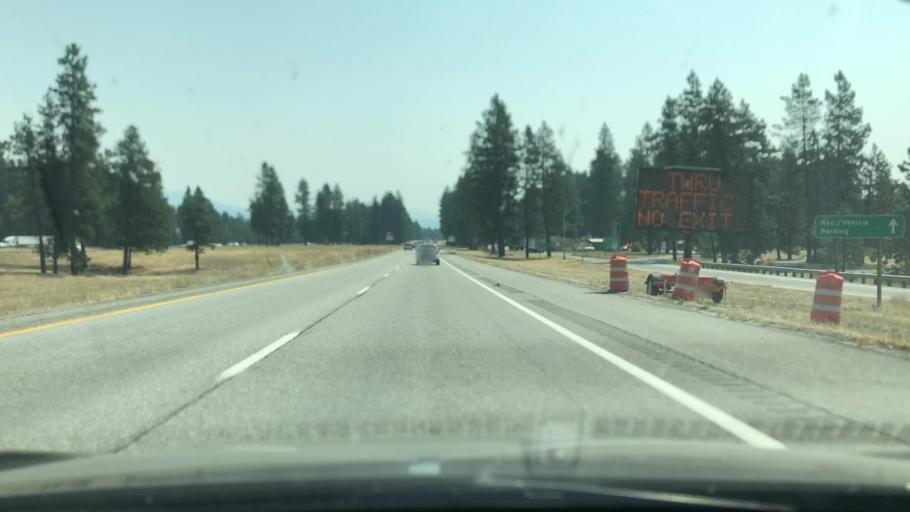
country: US
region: Idaho
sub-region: Kootenai County
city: Post Falls
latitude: 47.7086
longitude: -116.8703
